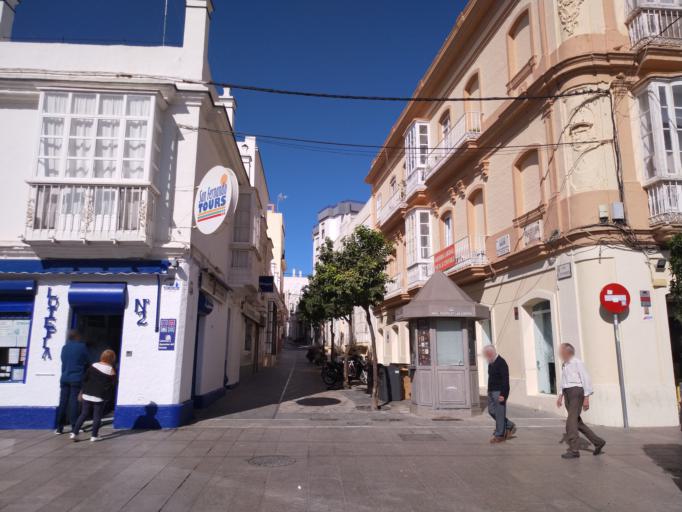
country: ES
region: Andalusia
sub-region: Provincia de Cadiz
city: San Fernando
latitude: 36.4651
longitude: -6.1974
